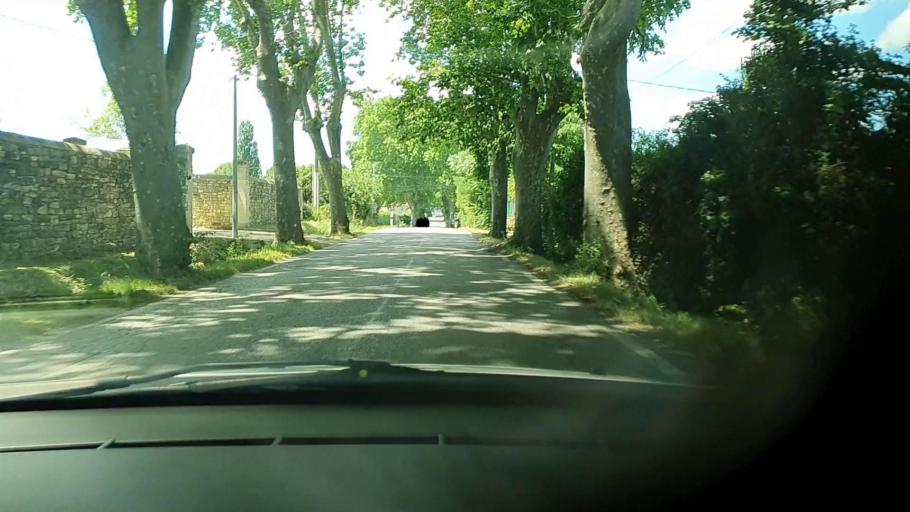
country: FR
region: Languedoc-Roussillon
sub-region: Departement du Gard
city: Montaren-et-Saint-Mediers
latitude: 44.0256
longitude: 4.3866
